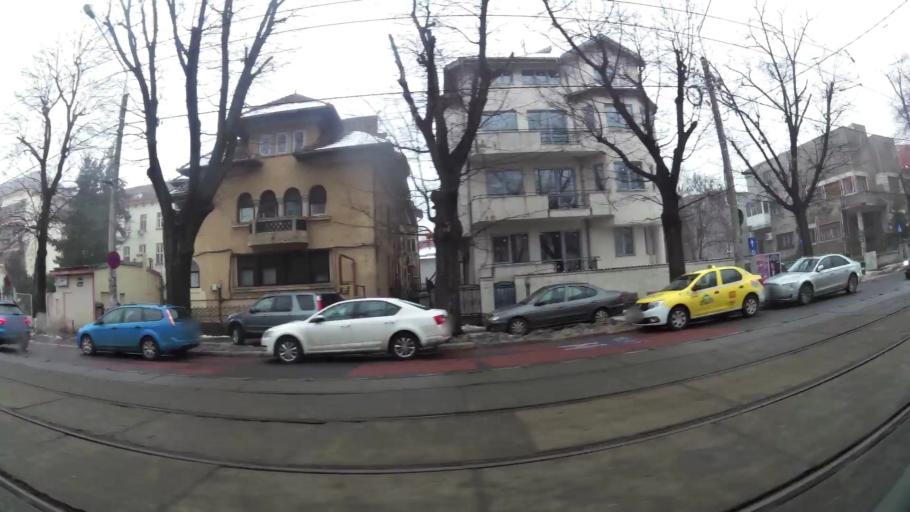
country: RO
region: Bucuresti
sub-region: Municipiul Bucuresti
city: Bucuresti
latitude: 44.4671
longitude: 26.0746
